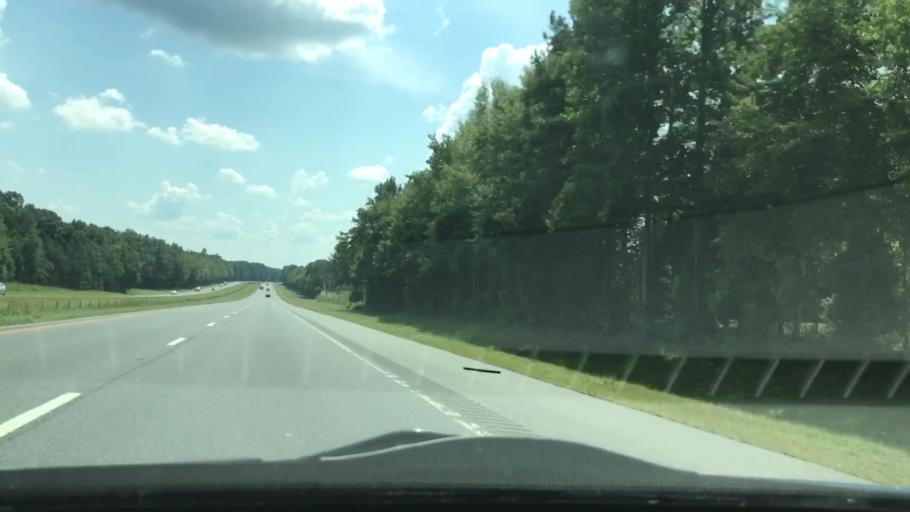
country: US
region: North Carolina
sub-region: Randolph County
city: Randleman
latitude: 35.8667
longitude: -79.8185
